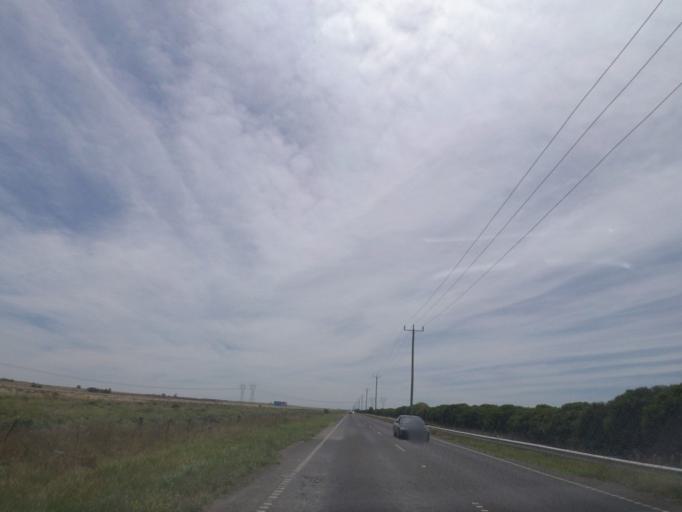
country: AU
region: Victoria
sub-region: Melton
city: Caroline Springs
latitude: -37.7738
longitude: 144.7006
